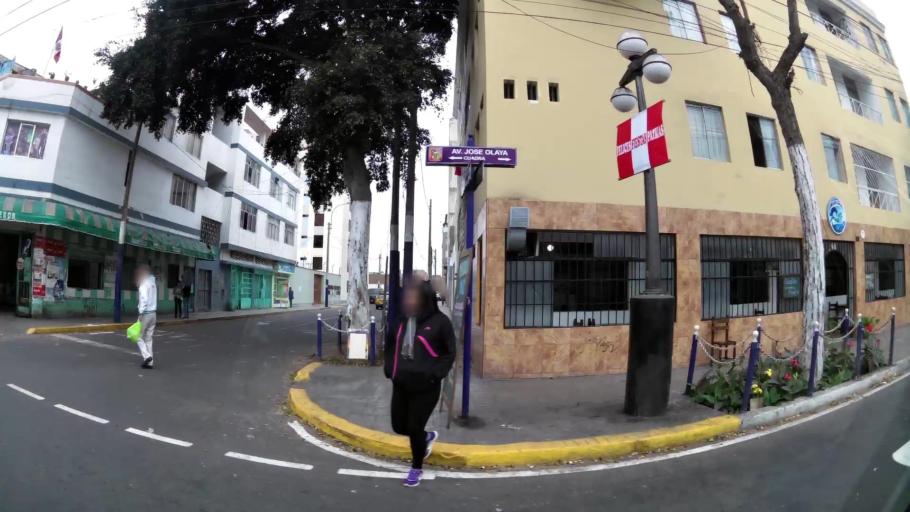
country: PE
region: Lima
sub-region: Lima
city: Surco
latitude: -12.1653
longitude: -77.0237
